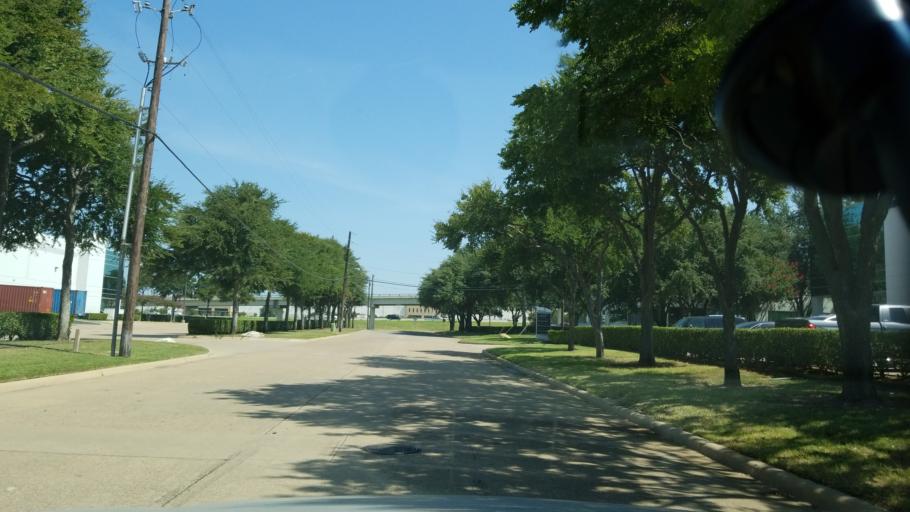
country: US
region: Texas
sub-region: Dallas County
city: Farmers Branch
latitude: 32.9053
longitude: -96.9024
